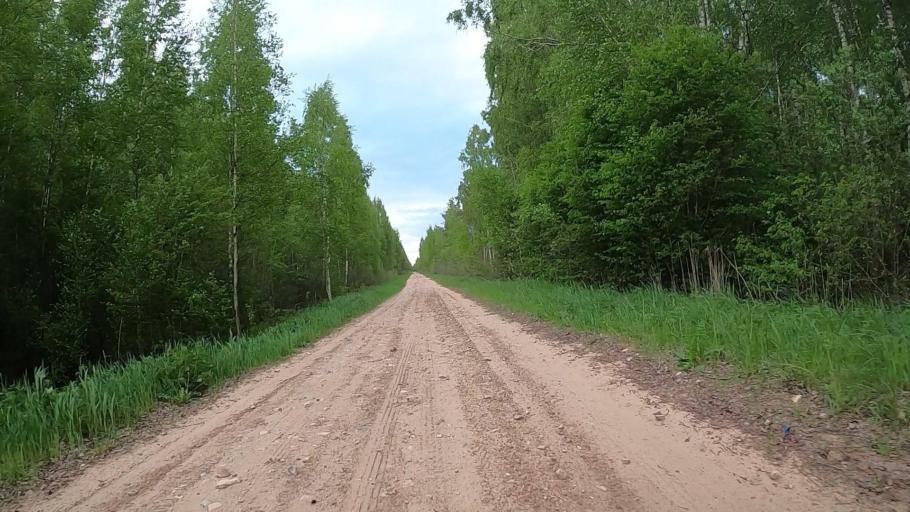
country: LV
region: Olaine
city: Olaine
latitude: 56.8369
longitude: 23.9249
